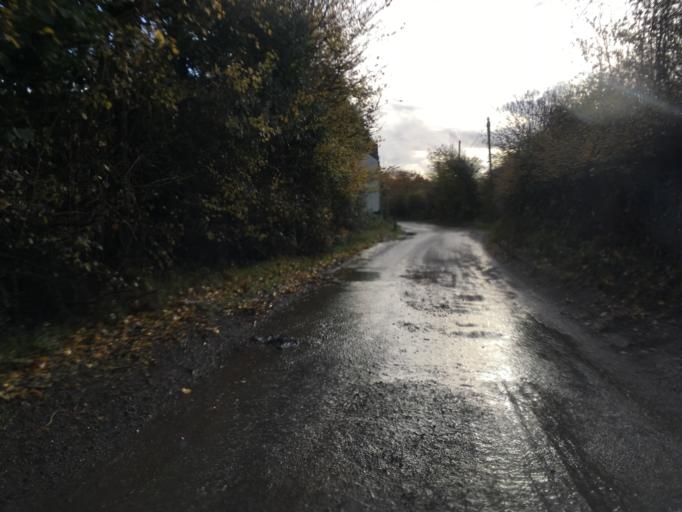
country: GB
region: England
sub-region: South Gloucestershire
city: Siston
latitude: 51.4965
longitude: -2.4569
